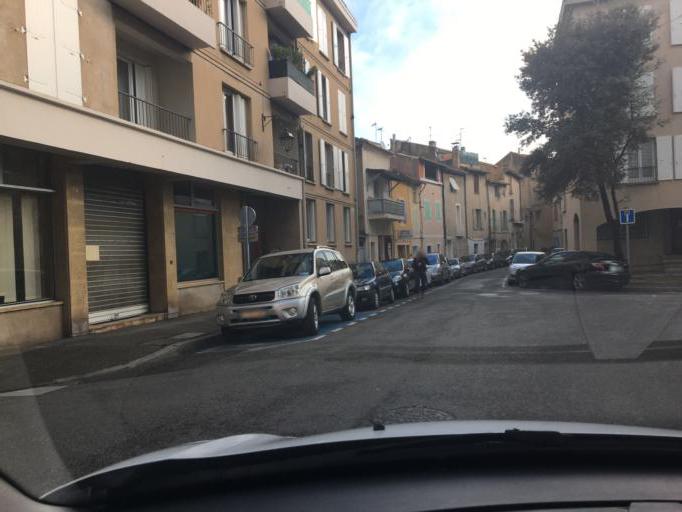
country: FR
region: Provence-Alpes-Cote d'Azur
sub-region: Departement du Vaucluse
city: Cavaillon
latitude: 43.8361
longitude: 5.0394
